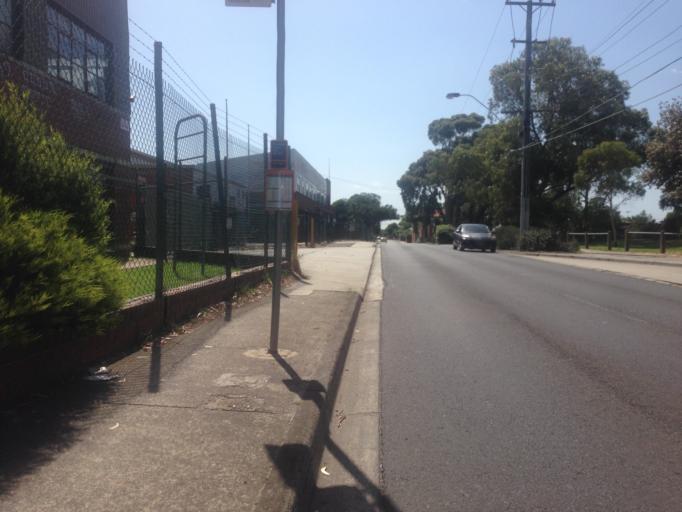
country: AU
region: Victoria
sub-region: Darebin
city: Fairfield
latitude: -37.7712
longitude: 145.0150
